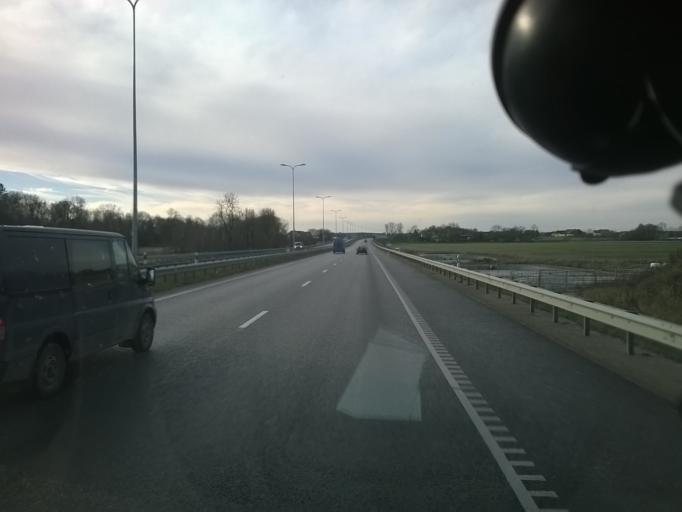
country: EE
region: Harju
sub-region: Kiili vald
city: Kiili
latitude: 59.3428
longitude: 24.8486
